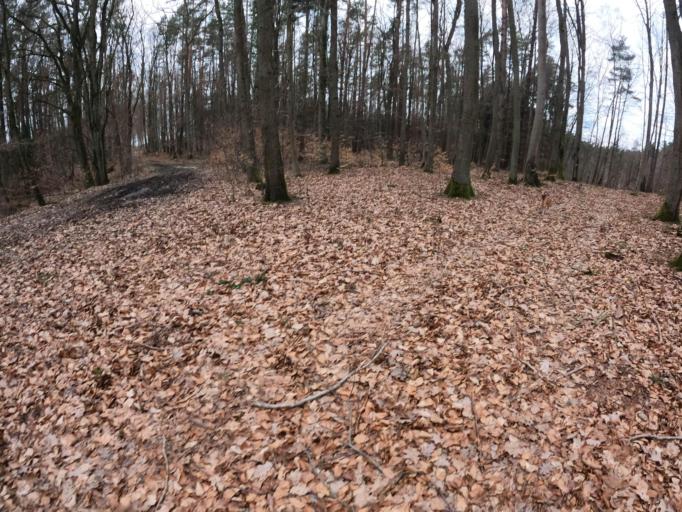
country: PL
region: West Pomeranian Voivodeship
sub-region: Powiat kamienski
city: Golczewo
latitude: 53.8194
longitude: 15.0214
